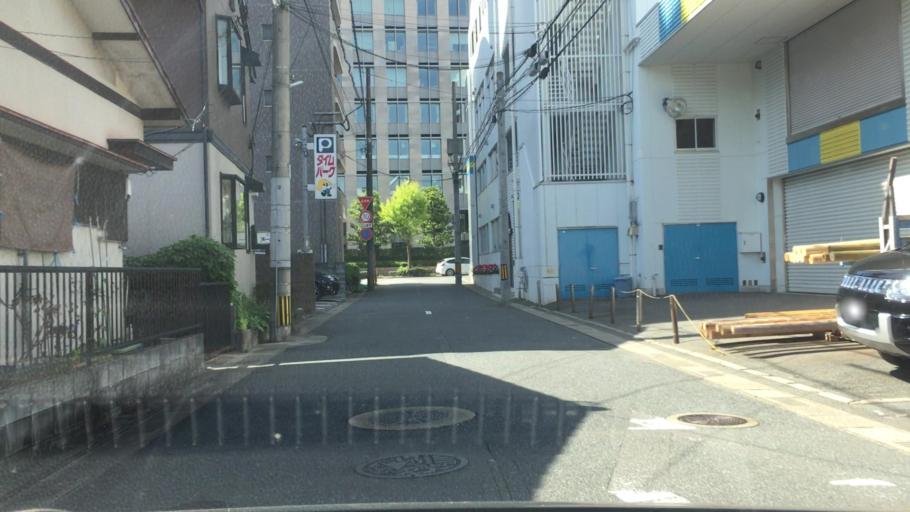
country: JP
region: Fukuoka
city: Fukuoka-shi
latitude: 33.5736
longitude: 130.3669
